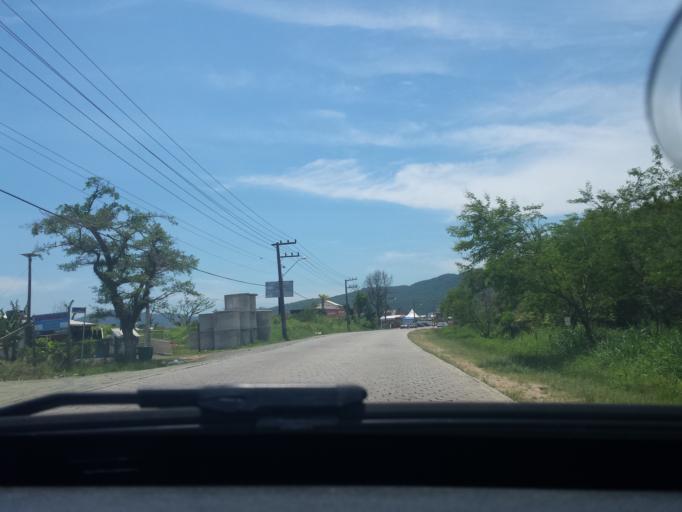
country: BR
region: Santa Catarina
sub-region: Porto Belo
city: Porto Belo
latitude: -27.1572
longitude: -48.5866
